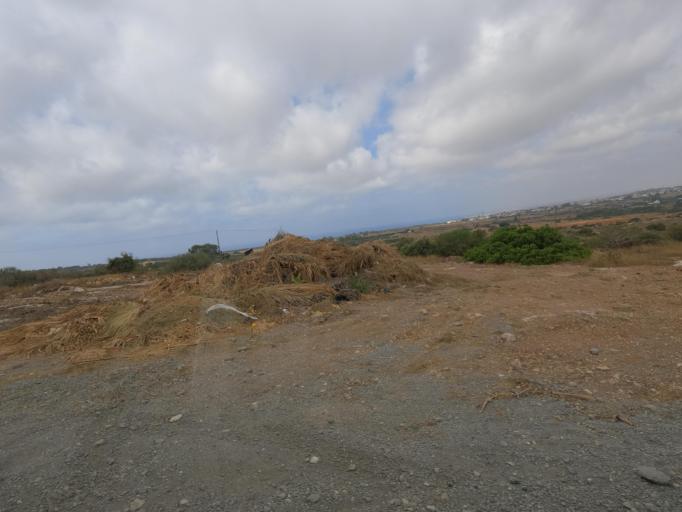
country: CY
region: Ammochostos
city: Protaras
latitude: 35.0059
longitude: 34.0269
